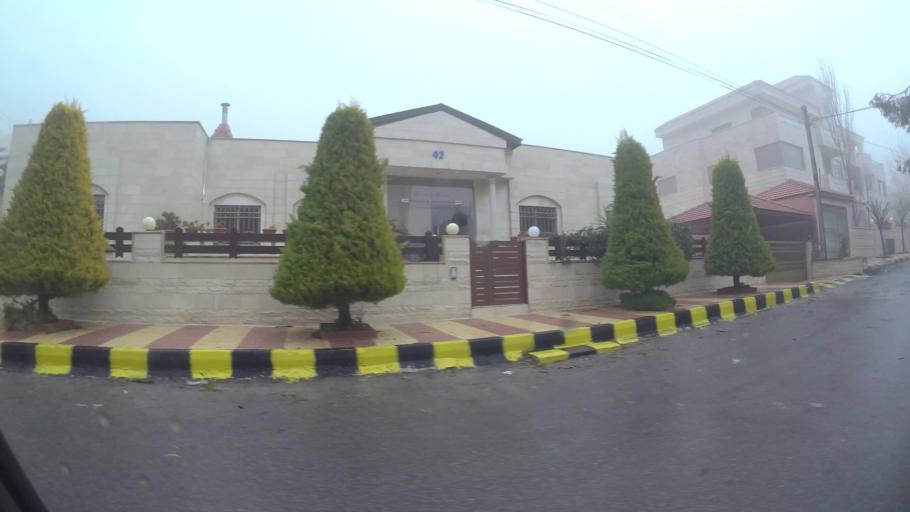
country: JO
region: Amman
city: Al Jubayhah
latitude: 32.0164
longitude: 35.8365
